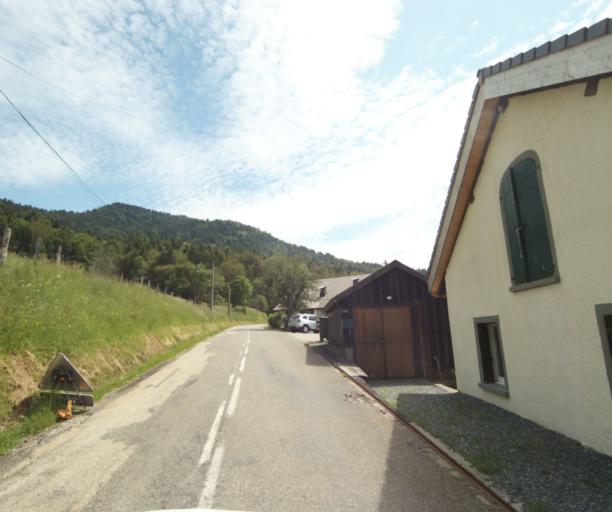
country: FR
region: Rhone-Alpes
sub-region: Departement de la Haute-Savoie
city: Perrignier
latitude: 46.2888
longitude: 6.4758
